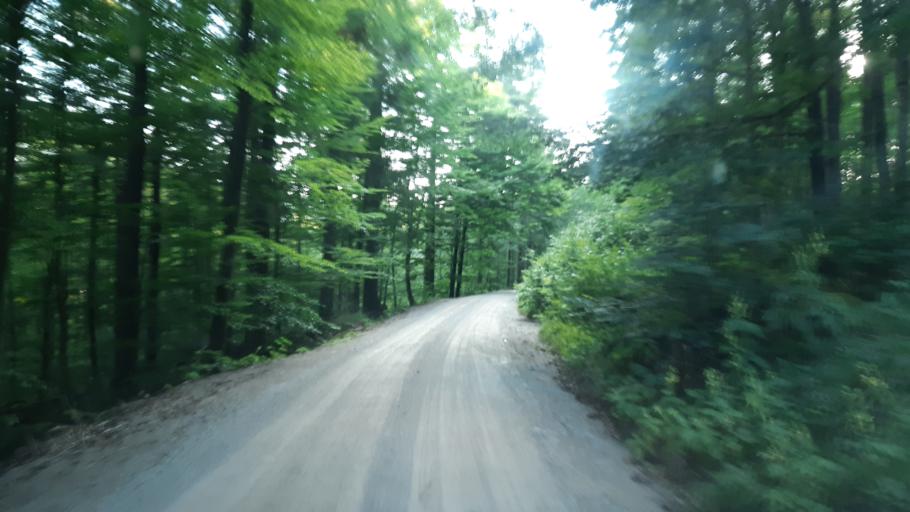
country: SI
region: Kocevje
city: Kocevje
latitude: 45.6669
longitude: 14.9688
